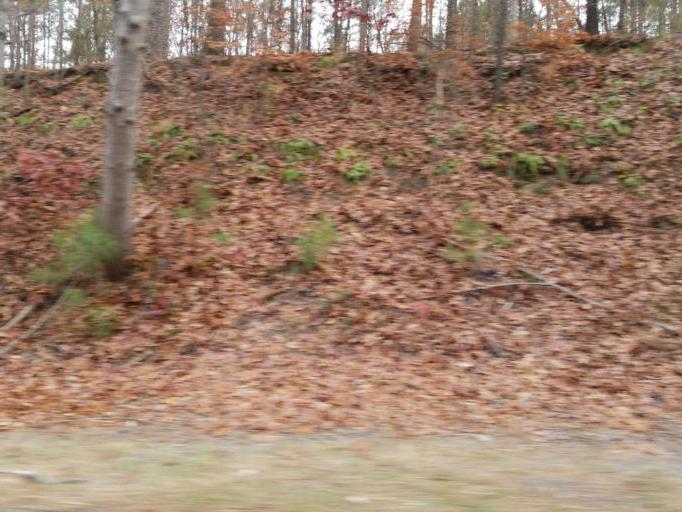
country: US
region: Georgia
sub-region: Cherokee County
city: Holly Springs
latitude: 34.2138
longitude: -84.5470
